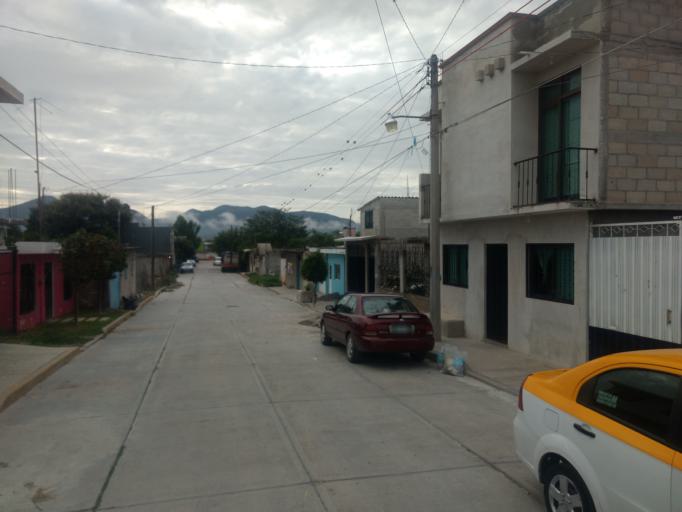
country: MX
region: Oaxaca
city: Ciudad de Huajuapam de Leon
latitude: 17.8060
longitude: -97.7904
